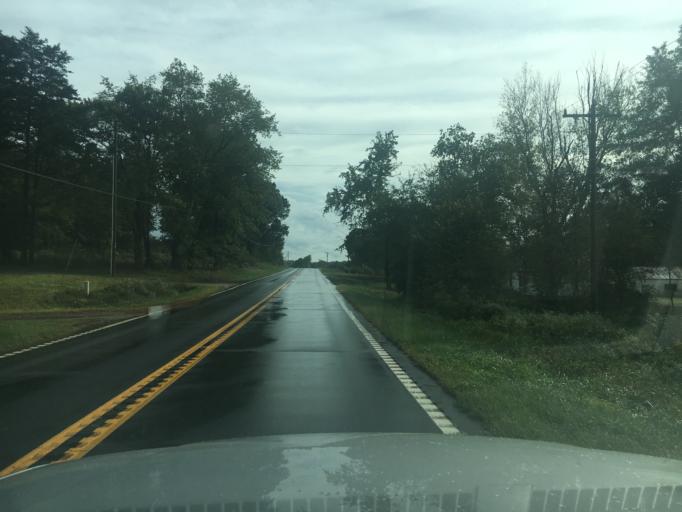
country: US
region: North Carolina
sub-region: Rutherford County
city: Spindale
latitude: 35.4463
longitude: -81.8903
